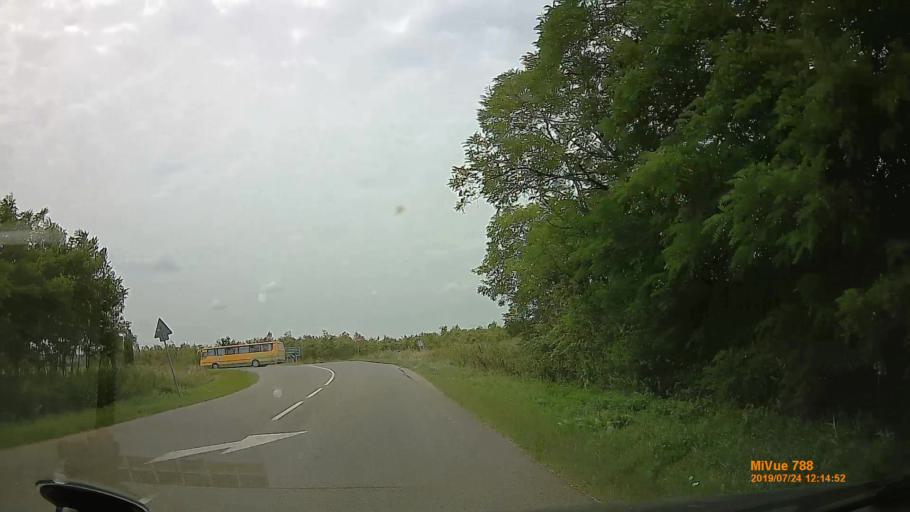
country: HU
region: Szabolcs-Szatmar-Bereg
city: Vasarosnameny
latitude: 48.1883
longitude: 22.3446
